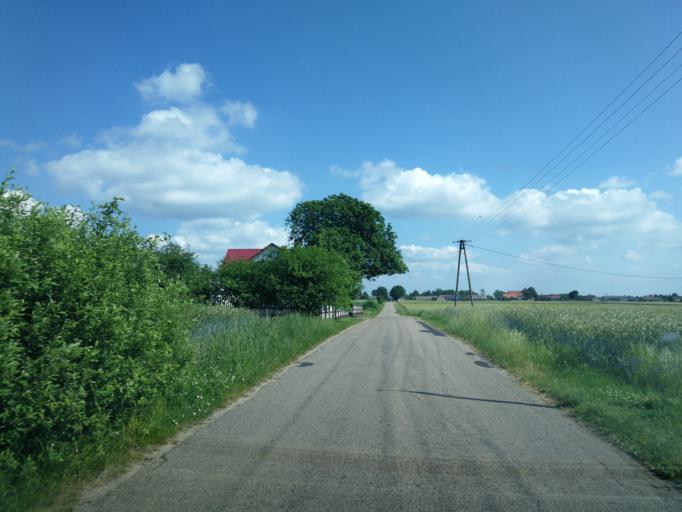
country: PL
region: Warmian-Masurian Voivodeship
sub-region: Powiat dzialdowski
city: Lidzbark
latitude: 53.3137
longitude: 19.8544
